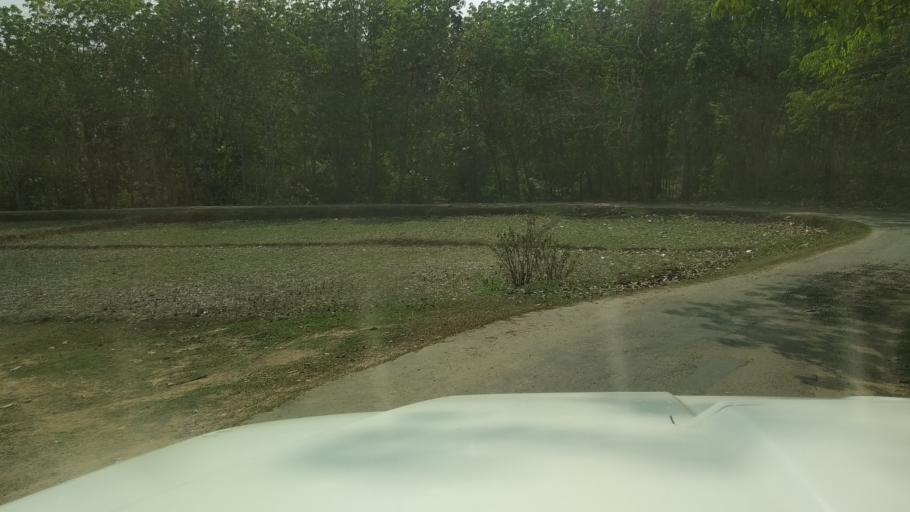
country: IN
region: Tripura
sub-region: West Tripura
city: Sonamura
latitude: 23.4286
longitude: 91.3178
